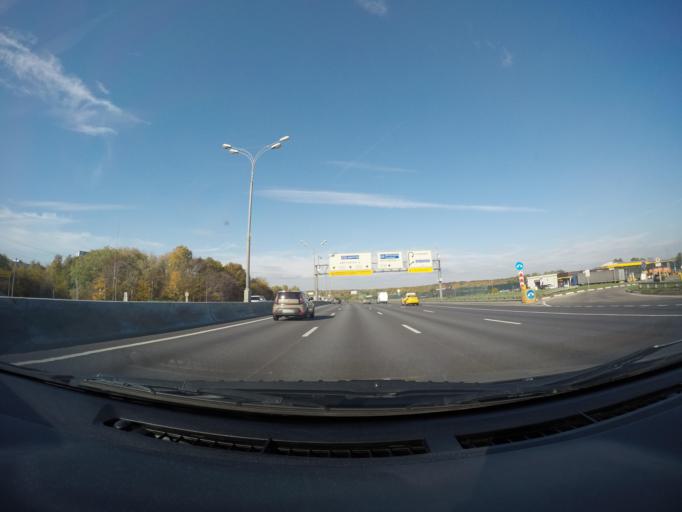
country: RU
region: Moscow
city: Gol'yanovo
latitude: 55.8253
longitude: 37.8345
